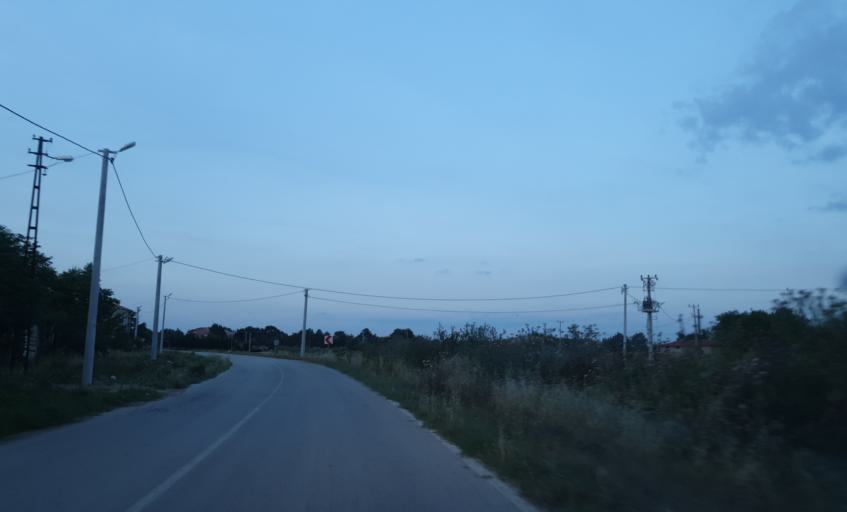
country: TR
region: Tekirdag
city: Beyazkoy
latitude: 41.4354
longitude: 27.6952
